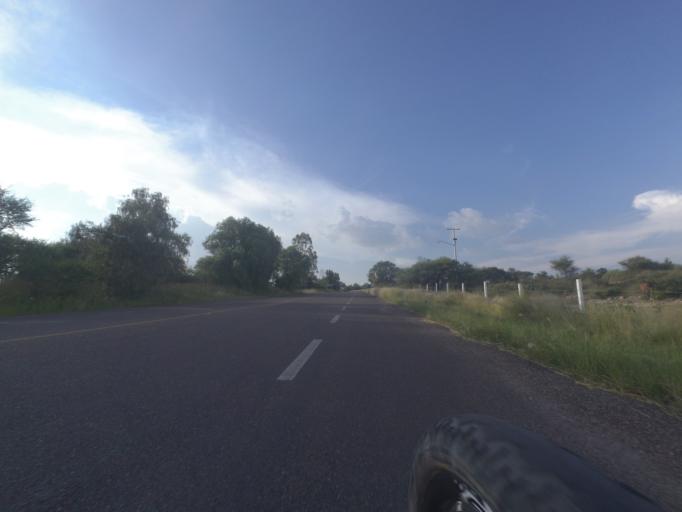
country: MX
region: Aguascalientes
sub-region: Aguascalientes
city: Penuelas (El Cienegal)
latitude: 21.7615
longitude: -102.3512
